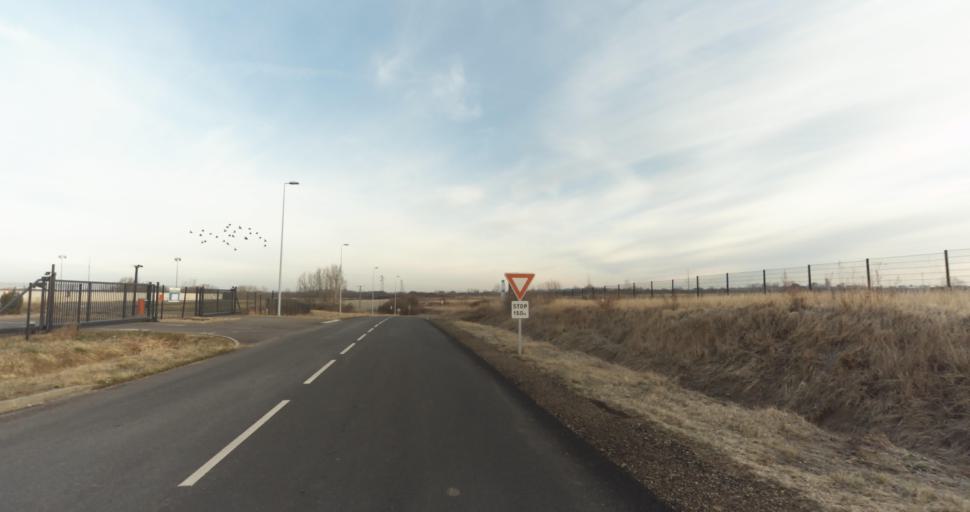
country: FR
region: Lorraine
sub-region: Departement de Meurthe-et-Moselle
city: Giraumont
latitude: 49.1582
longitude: 5.9032
